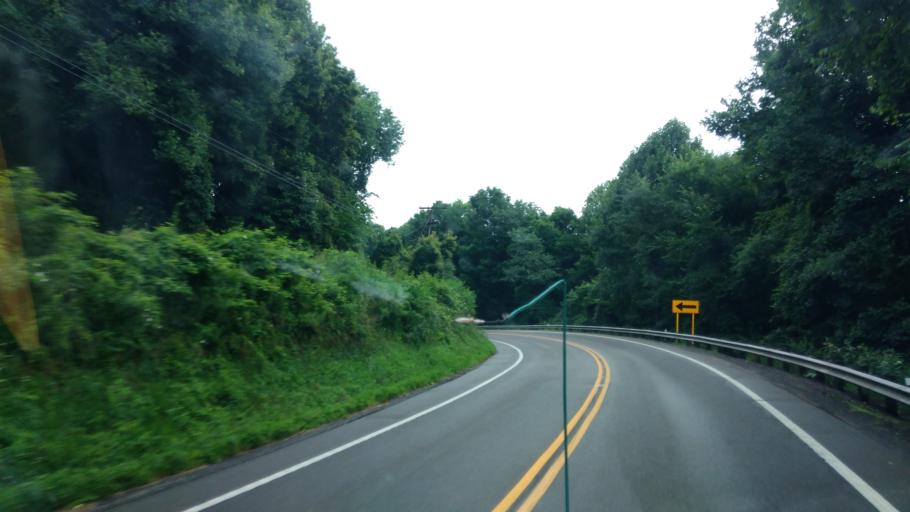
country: US
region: Ohio
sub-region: Stark County
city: Minerva
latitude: 40.6962
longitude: -81.0114
